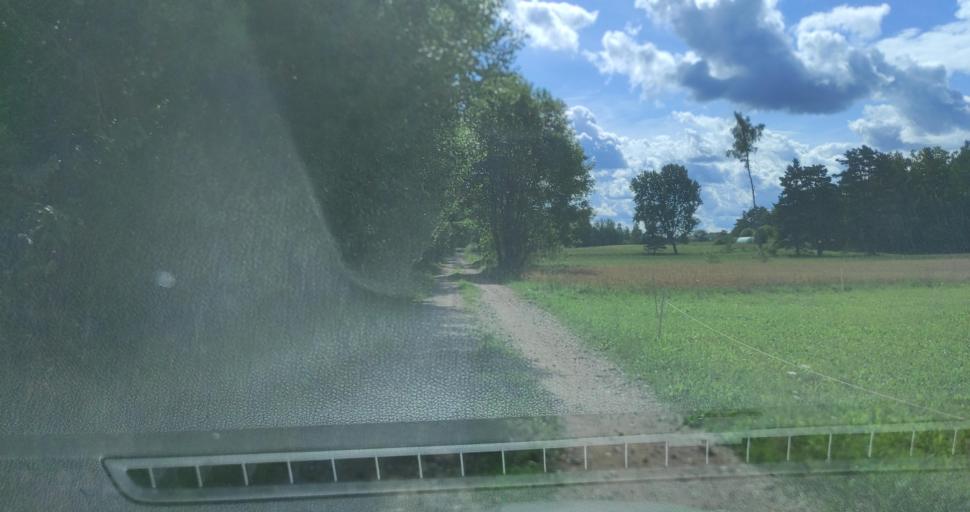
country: LV
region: Alsunga
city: Alsunga
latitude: 57.0283
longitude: 21.7002
